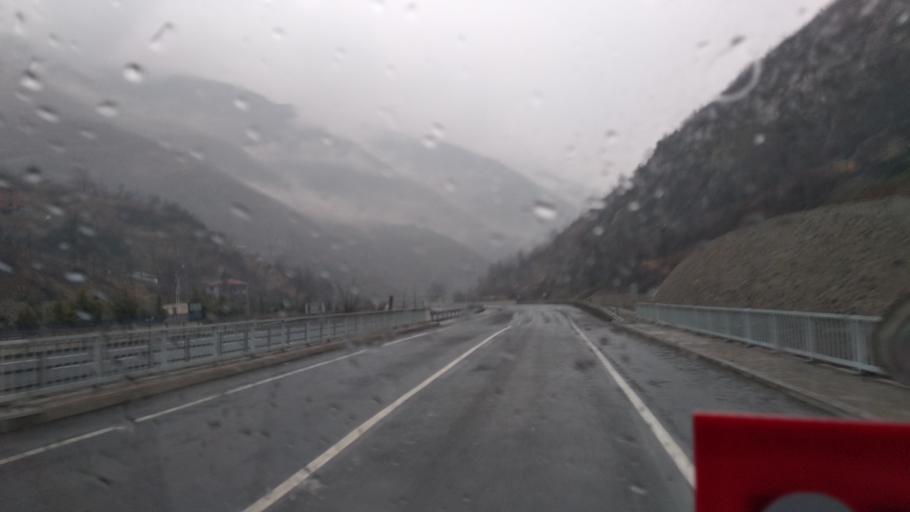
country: TR
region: Trabzon
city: Macka
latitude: 40.7954
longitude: 39.5836
